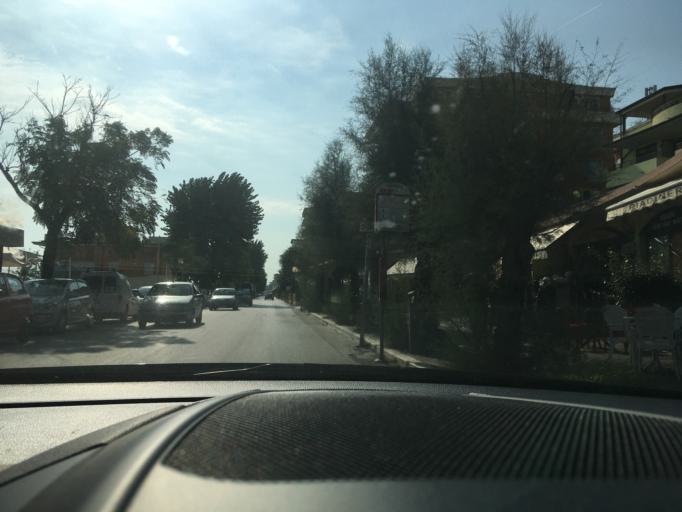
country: IT
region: Emilia-Romagna
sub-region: Provincia di Rimini
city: Bellaria-Igea Marina
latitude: 44.1114
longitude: 12.5073
